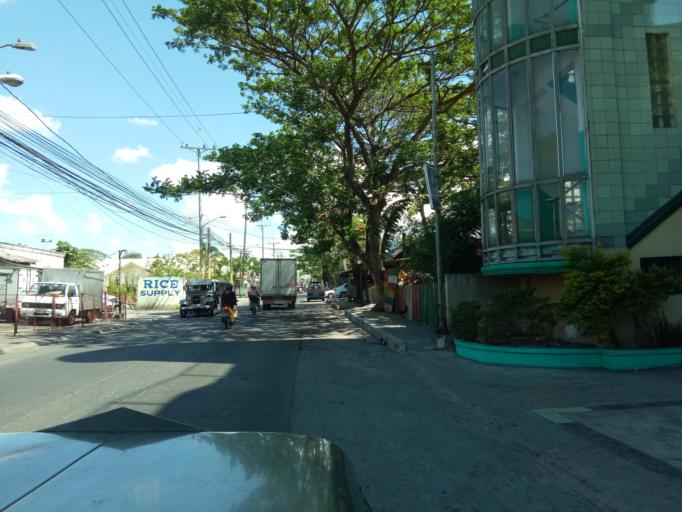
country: PH
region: Calabarzon
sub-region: Province of Cavite
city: Dasmarinas
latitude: 14.3432
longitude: 120.9473
